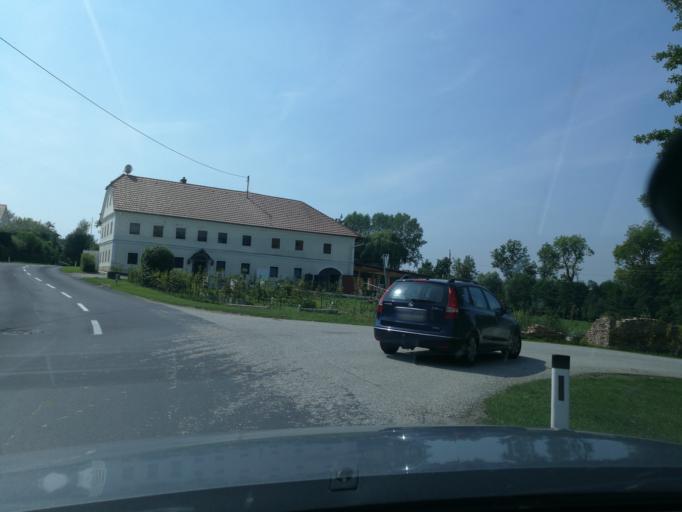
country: AT
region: Upper Austria
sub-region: Politischer Bezirk Grieskirchen
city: Grieskirchen
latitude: 48.2875
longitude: 13.8109
